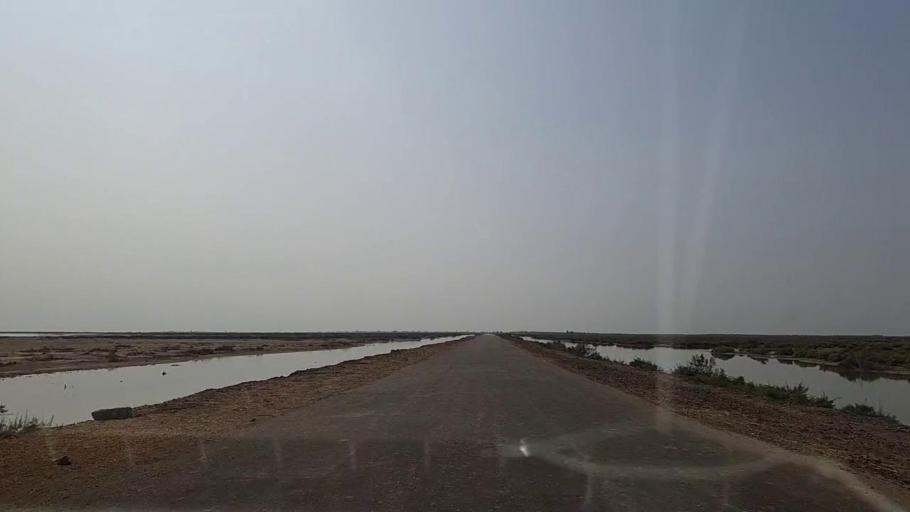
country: PK
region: Sindh
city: Chuhar Jamali
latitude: 24.2203
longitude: 67.8745
